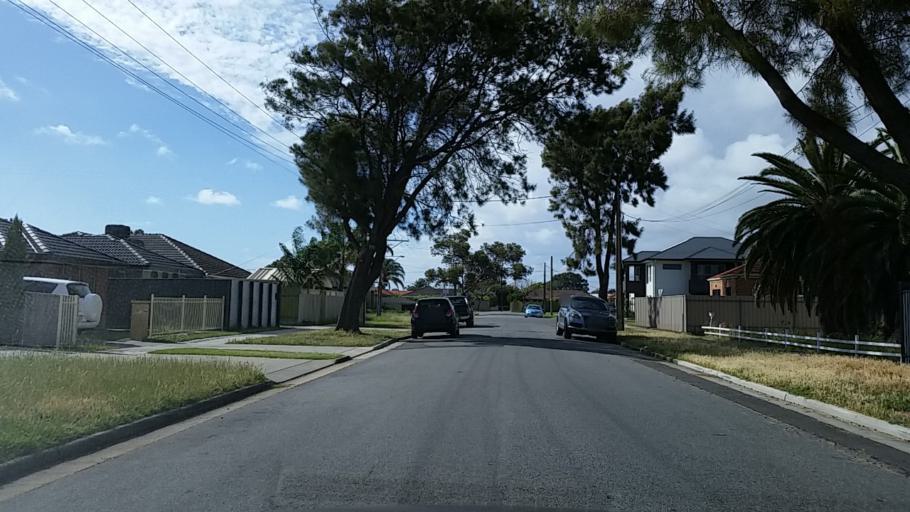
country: AU
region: South Australia
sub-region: Charles Sturt
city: Royal Park
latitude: -34.8864
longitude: 138.5093
